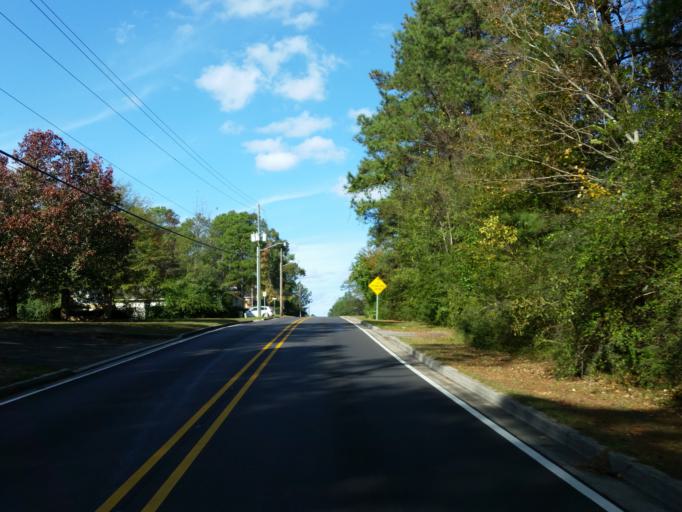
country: US
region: Mississippi
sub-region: Lamar County
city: West Hattiesburg
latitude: 31.3060
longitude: -89.3480
